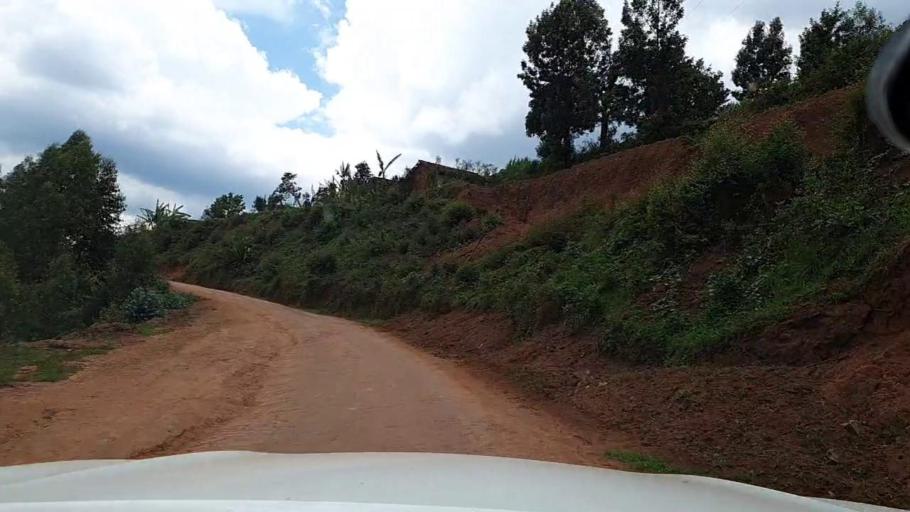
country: RW
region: Southern Province
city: Butare
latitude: -2.7072
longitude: 29.5482
